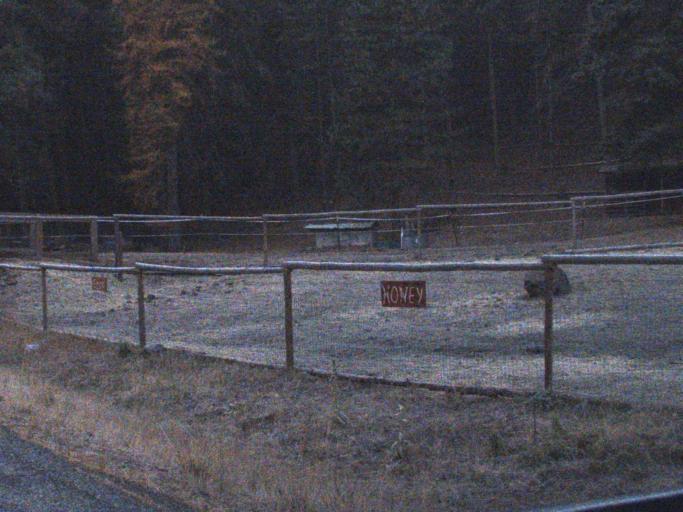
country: US
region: Washington
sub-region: Ferry County
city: Republic
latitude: 48.6035
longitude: -118.7389
